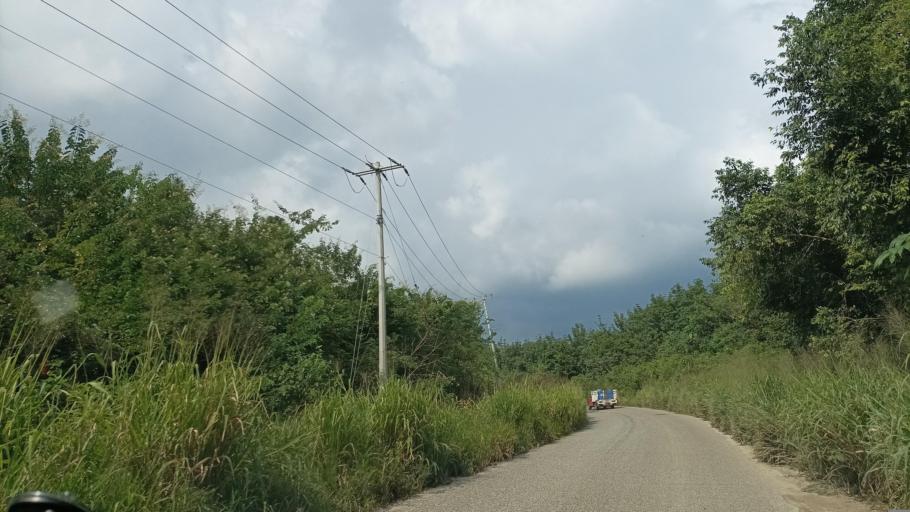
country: MX
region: Veracruz
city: Las Choapas
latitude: 17.8090
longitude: -94.1076
